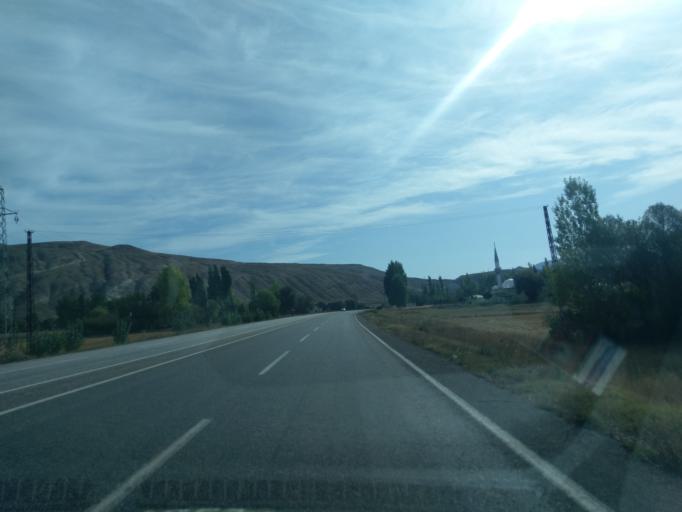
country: TR
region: Sivas
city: Zara
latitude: 39.8619
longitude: 37.8192
